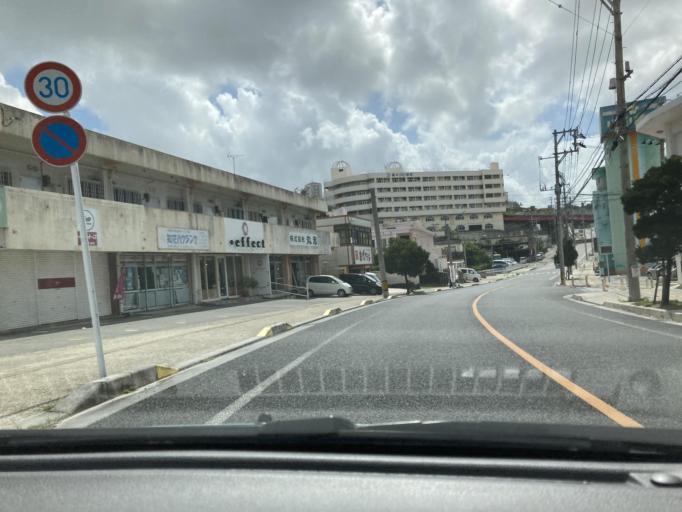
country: JP
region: Okinawa
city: Ginowan
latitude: 26.2617
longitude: 127.7290
